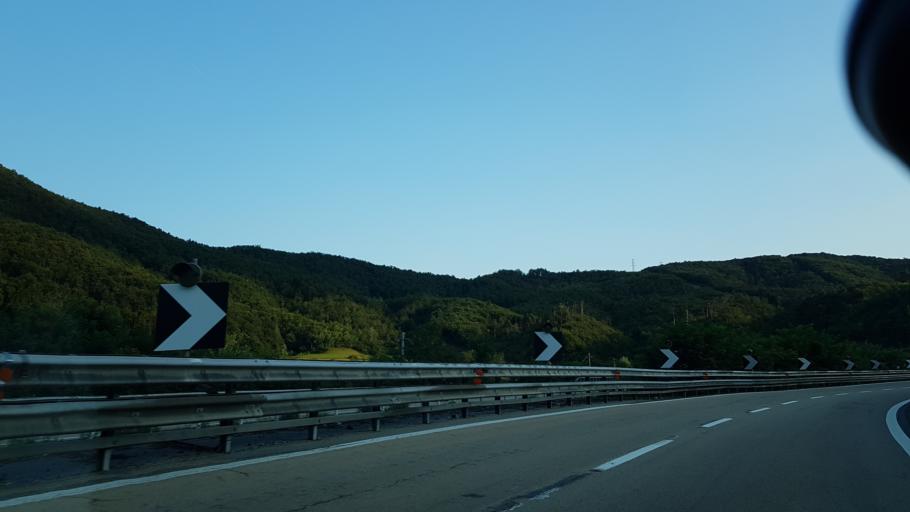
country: IT
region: Liguria
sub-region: Provincia di Genova
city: Ronco Scrivia
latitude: 44.5967
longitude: 8.9544
